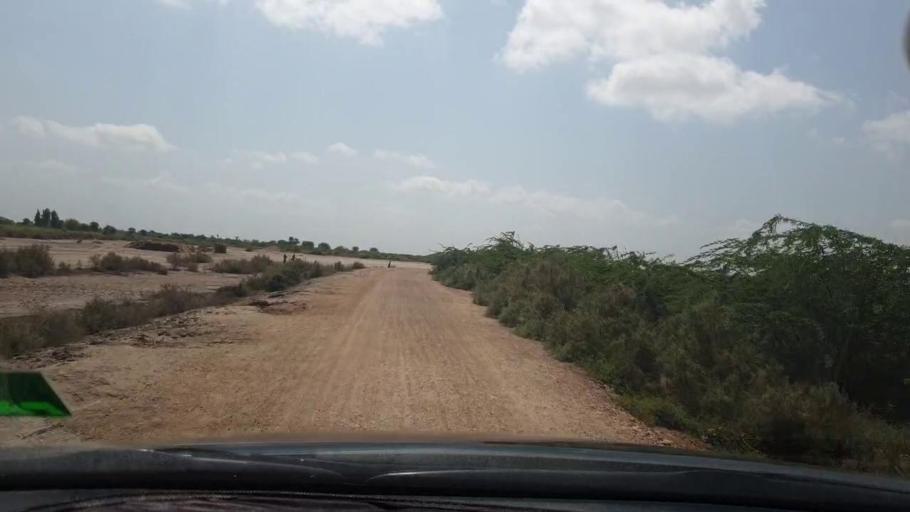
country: PK
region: Sindh
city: Tando Bago
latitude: 24.8633
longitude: 69.0892
